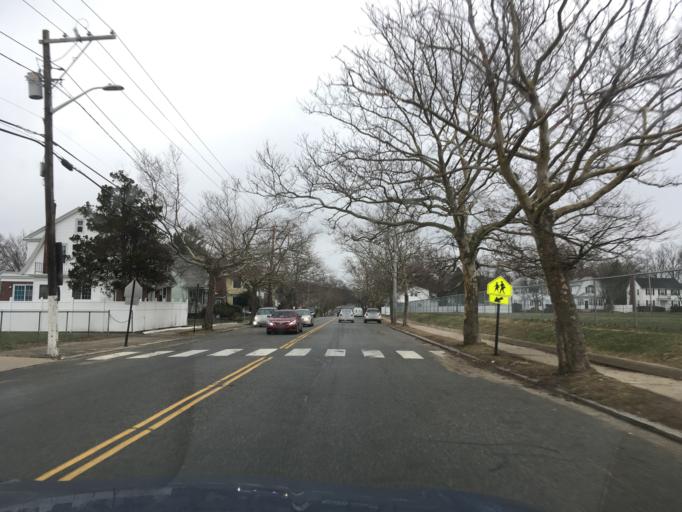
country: US
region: Rhode Island
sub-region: Providence County
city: North Providence
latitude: 41.8386
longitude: -71.4517
